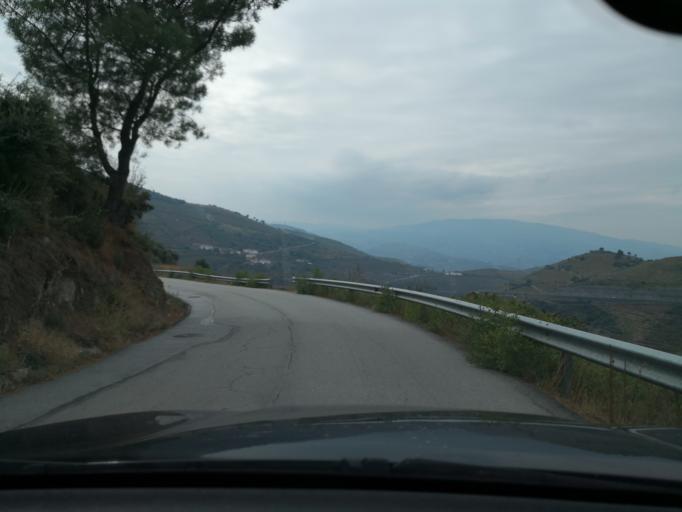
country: PT
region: Vila Real
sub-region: Peso da Regua
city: Peso da Regua
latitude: 41.1816
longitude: -7.7418
